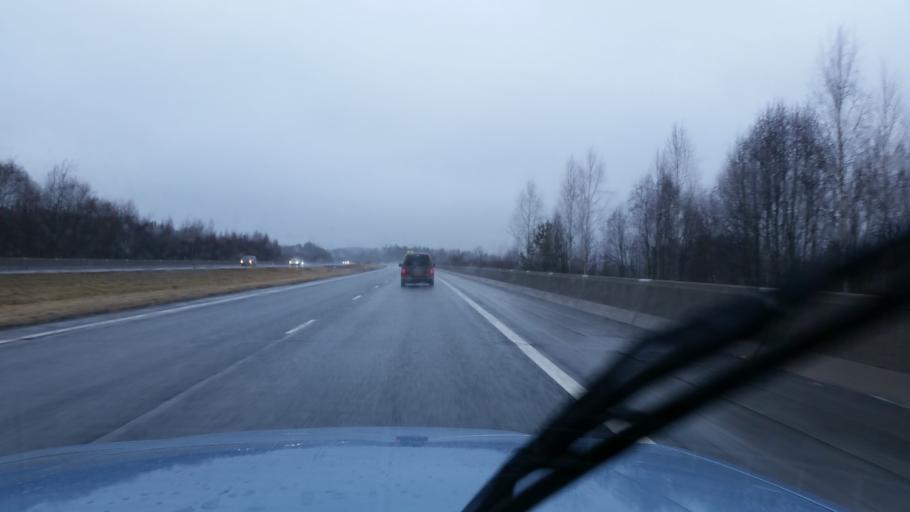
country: FI
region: Haeme
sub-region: Haemeenlinna
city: Parola
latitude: 61.0312
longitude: 24.3929
